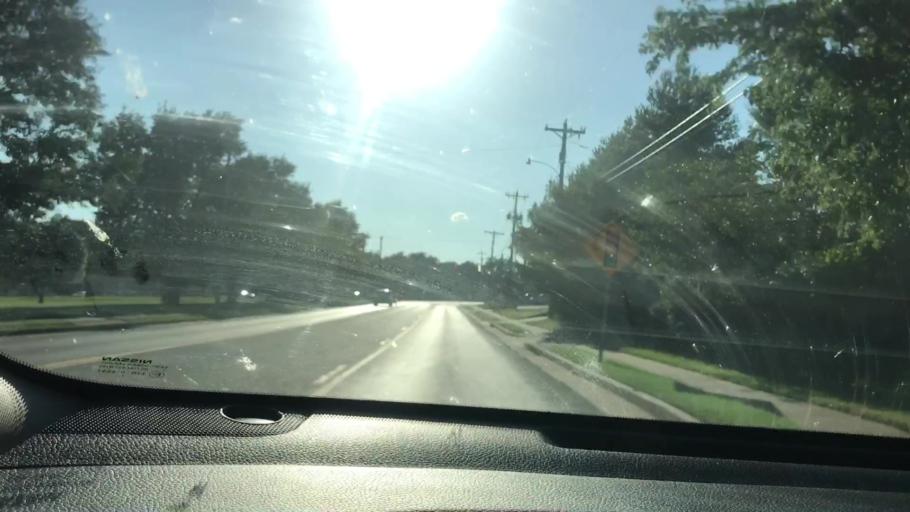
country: US
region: Kentucky
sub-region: Calloway County
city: Murray
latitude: 36.5956
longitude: -88.3136
